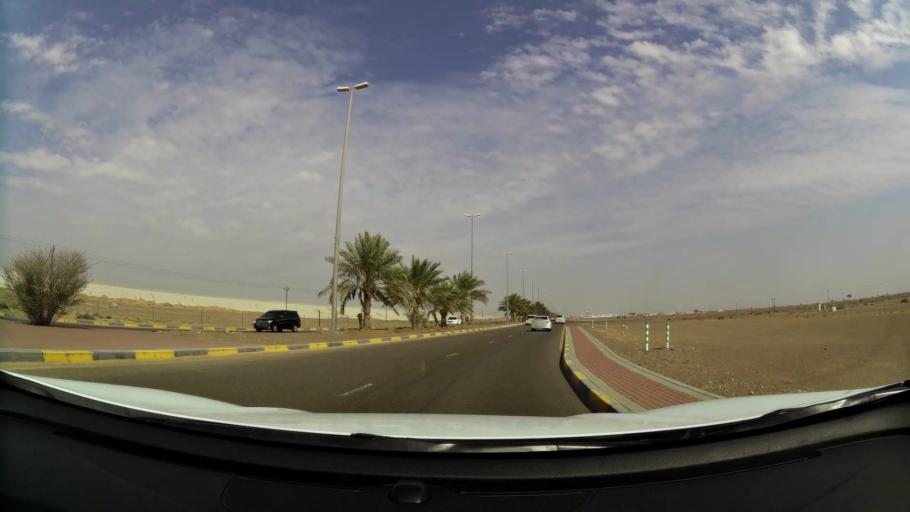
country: AE
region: Abu Dhabi
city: Al Ain
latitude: 24.0926
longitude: 55.8743
